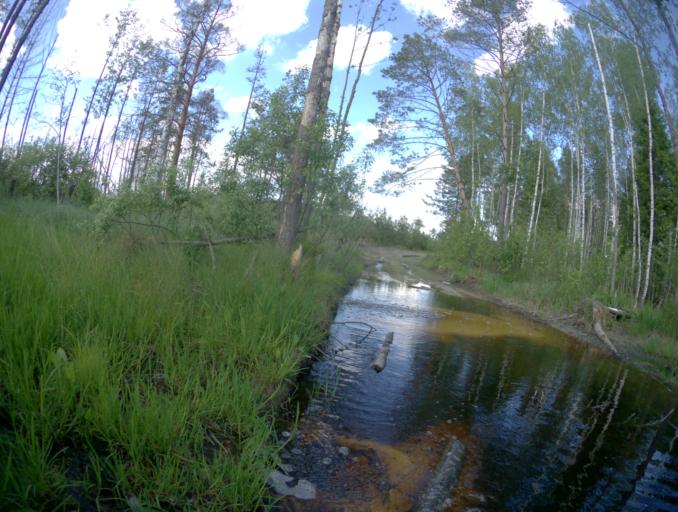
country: RU
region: Vladimir
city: Velikodvorskiy
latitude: 55.3184
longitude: 40.9246
